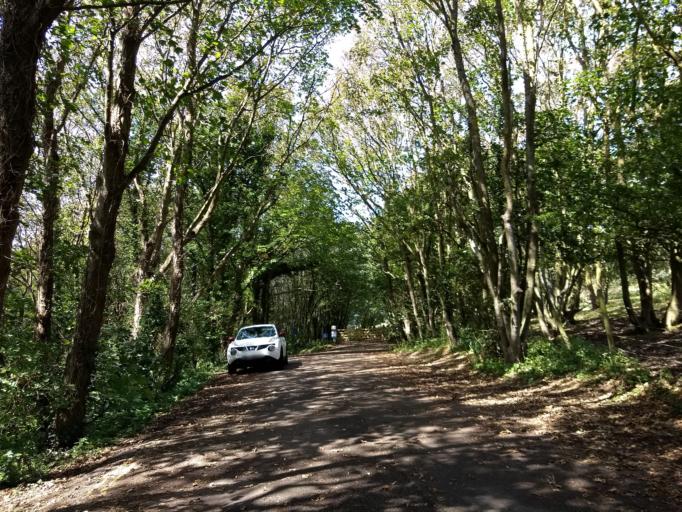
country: GB
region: England
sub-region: Isle of Wight
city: Totland
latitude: 50.6686
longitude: -1.5641
